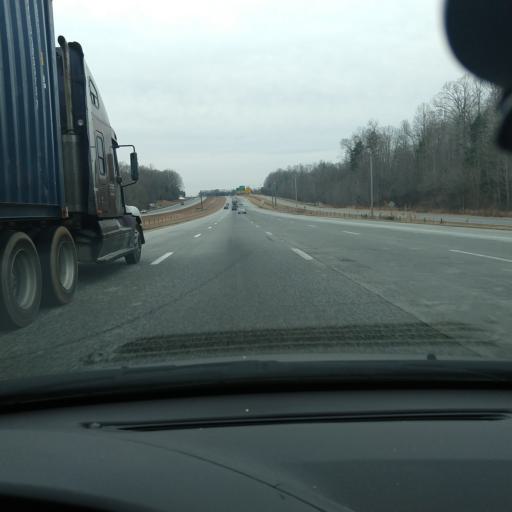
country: US
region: North Carolina
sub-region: Davidson County
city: Lexington
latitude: 35.8102
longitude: -80.2880
